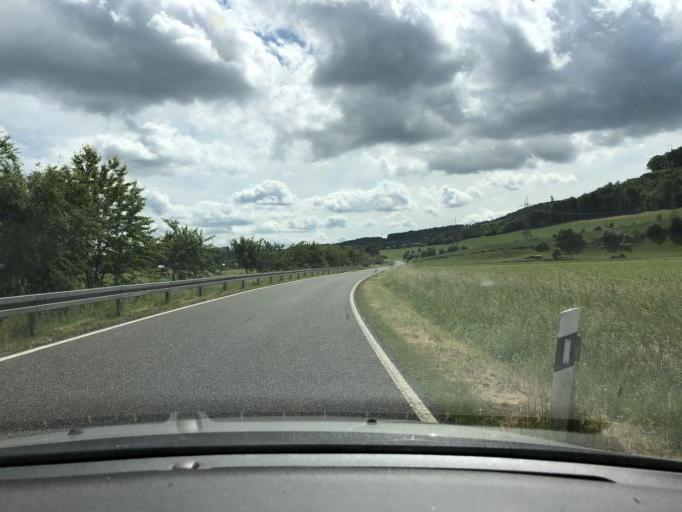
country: DE
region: Hesse
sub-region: Regierungsbezirk Kassel
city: Malsfeld
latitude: 51.0653
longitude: 9.5828
